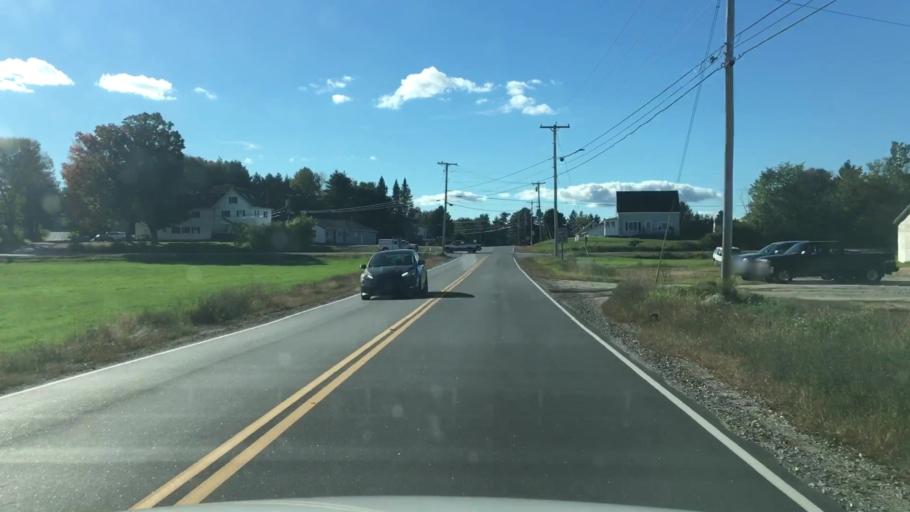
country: US
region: Maine
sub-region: Androscoggin County
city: Sabattus
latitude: 44.0758
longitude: -70.1134
